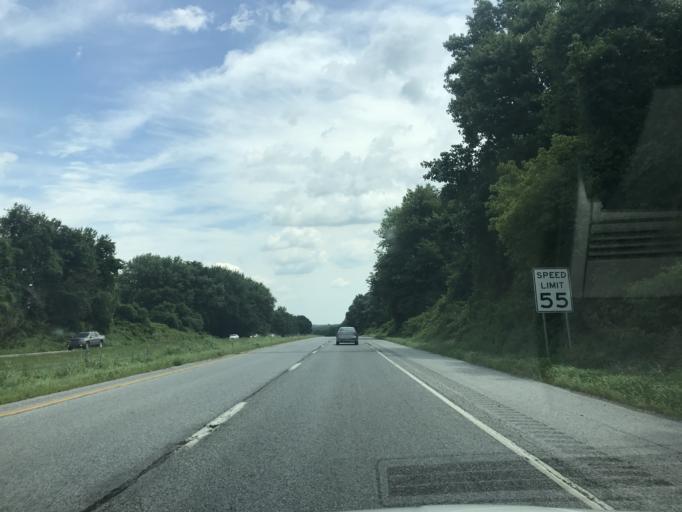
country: US
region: Pennsylvania
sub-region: Chester County
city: West Grove
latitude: 39.8260
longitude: -75.8570
